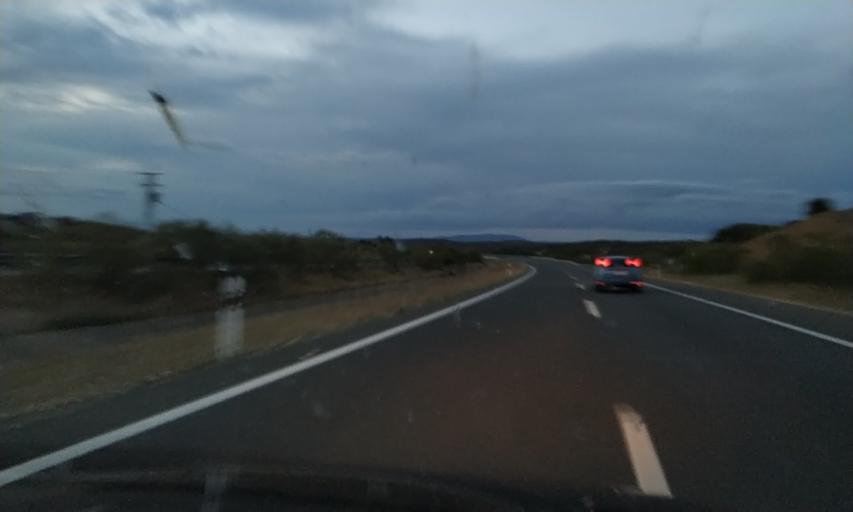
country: ES
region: Extremadura
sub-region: Provincia de Caceres
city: Casar de Caceres
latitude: 39.5992
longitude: -6.4060
